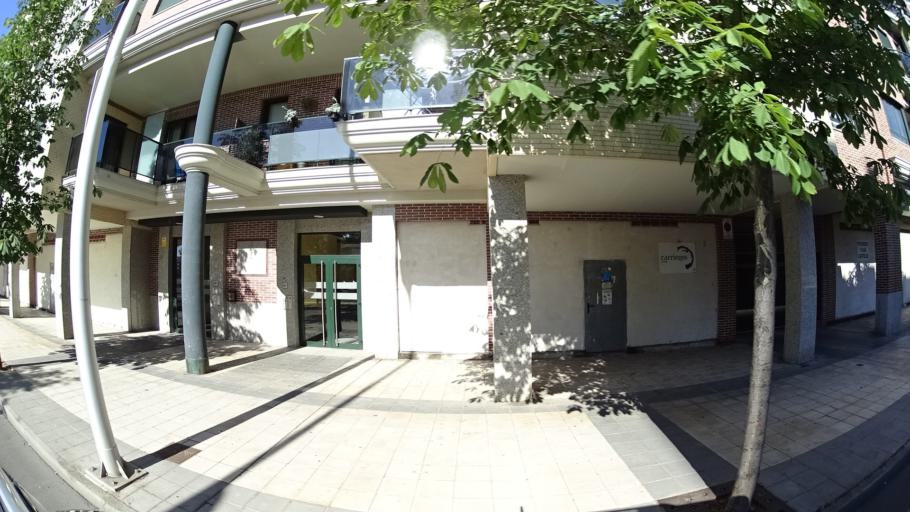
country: ES
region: Castille and Leon
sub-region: Provincia de Leon
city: Leon
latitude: 42.5859
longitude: -5.5654
